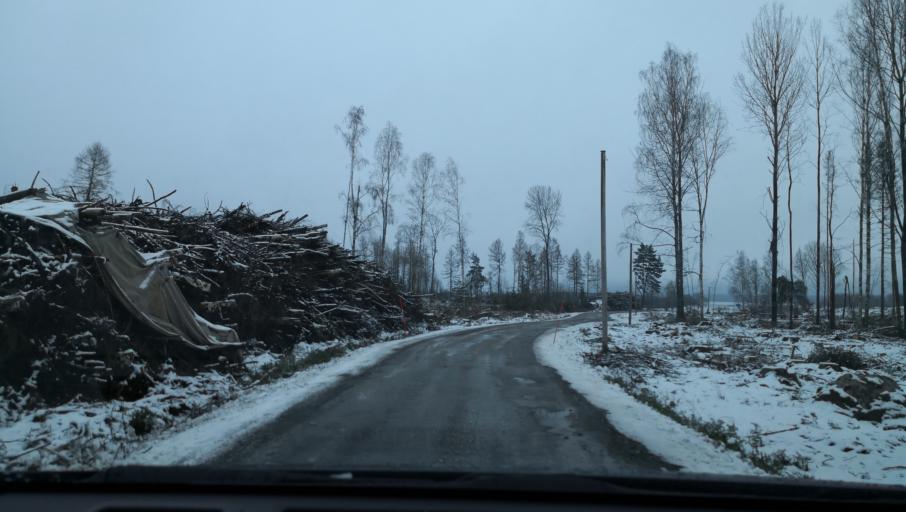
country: SE
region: Vaestmanland
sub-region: Kopings Kommun
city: Kolsva
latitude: 59.5447
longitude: 15.8808
